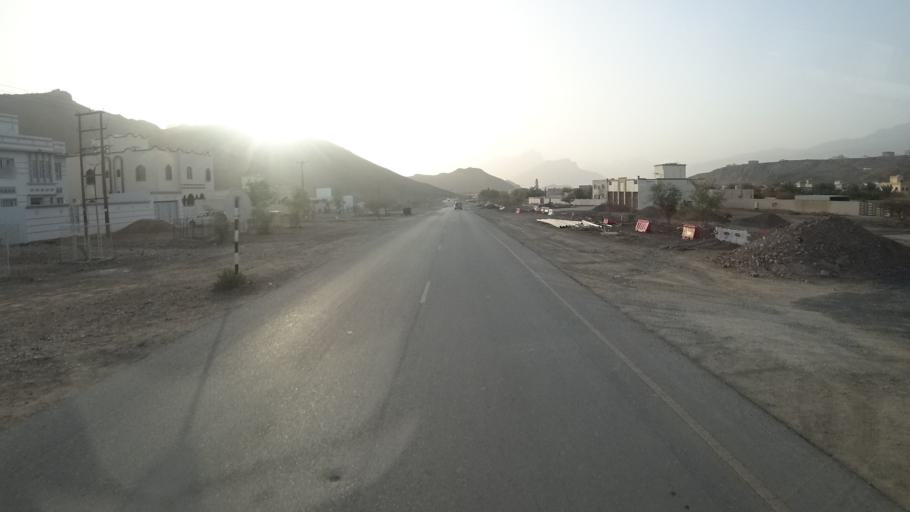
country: OM
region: Muhafazat ad Dakhiliyah
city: Bahla'
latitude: 23.0795
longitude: 57.3351
